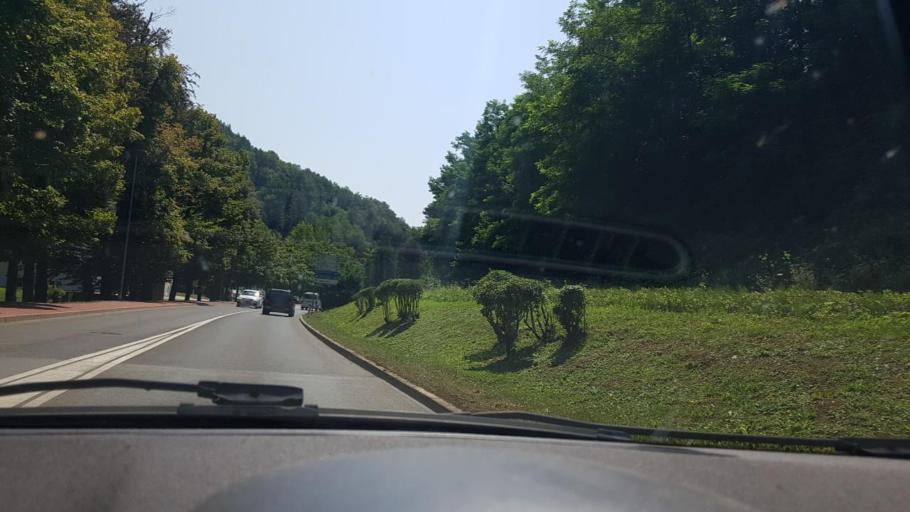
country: SI
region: Rogaska Slatina
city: Rogaska Slatina
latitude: 46.2371
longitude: 15.6354
